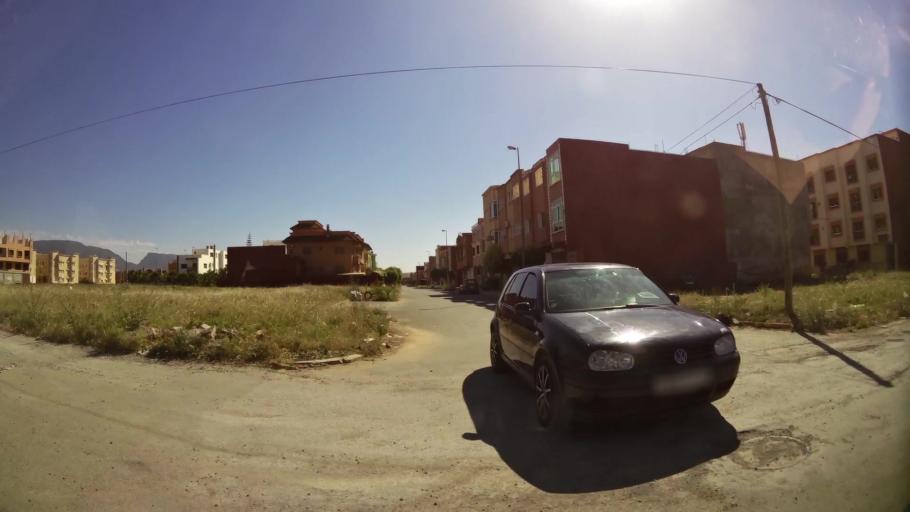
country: MA
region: Oriental
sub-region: Berkane-Taourirt
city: Berkane
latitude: 34.9430
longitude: -2.3370
